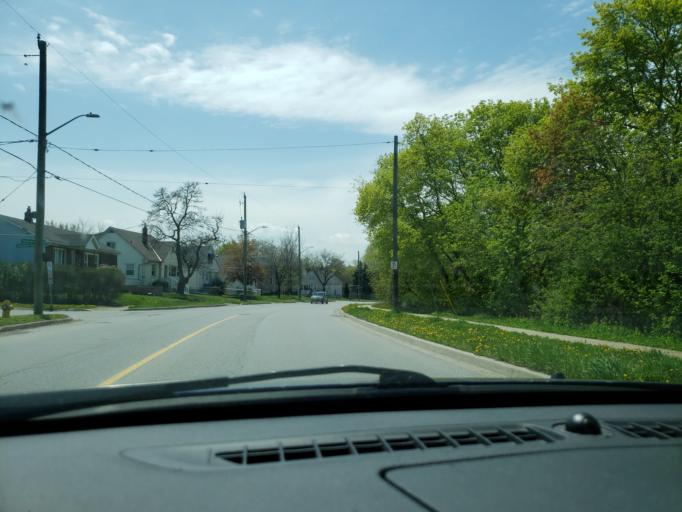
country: CA
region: Ontario
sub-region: Regional Municipality of Niagara
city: St. Catharines
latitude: 43.1599
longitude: -79.2257
